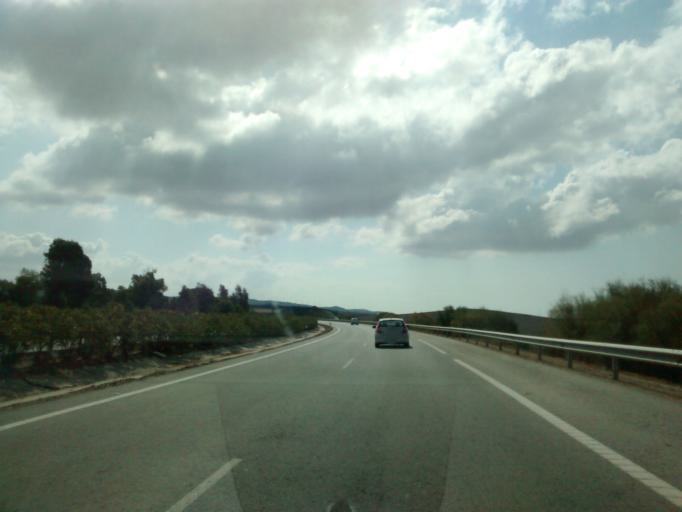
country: ES
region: Andalusia
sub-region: Provincia de Cadiz
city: Vejer de la Frontera
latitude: 36.2521
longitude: -6.0254
